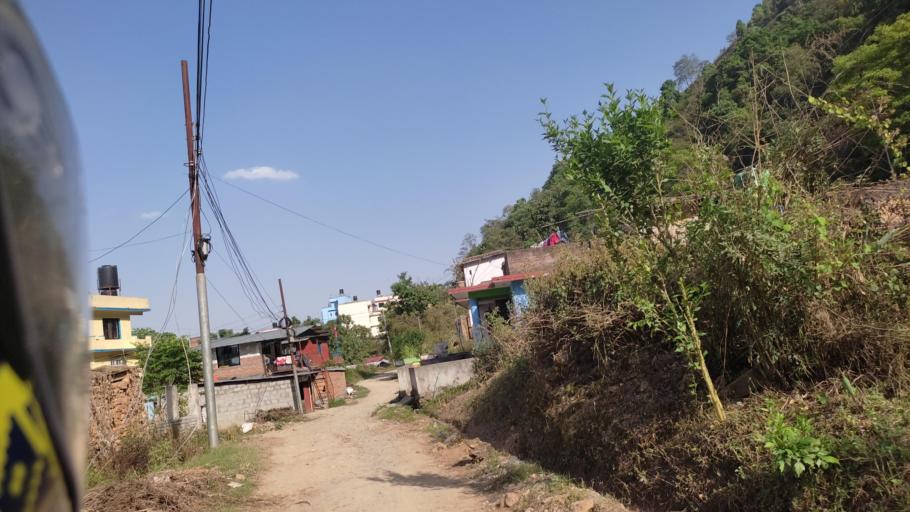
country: NP
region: Central Region
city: Kirtipur
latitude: 27.6570
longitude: 85.2656
